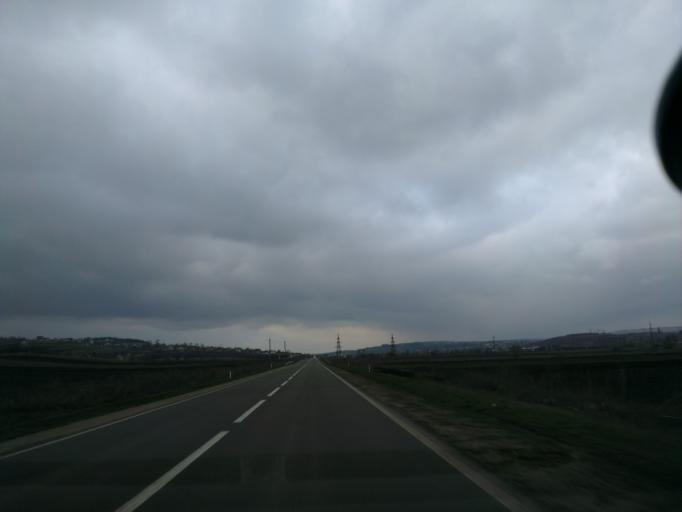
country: MD
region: Hincesti
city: Hincesti
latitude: 46.8044
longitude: 28.6117
